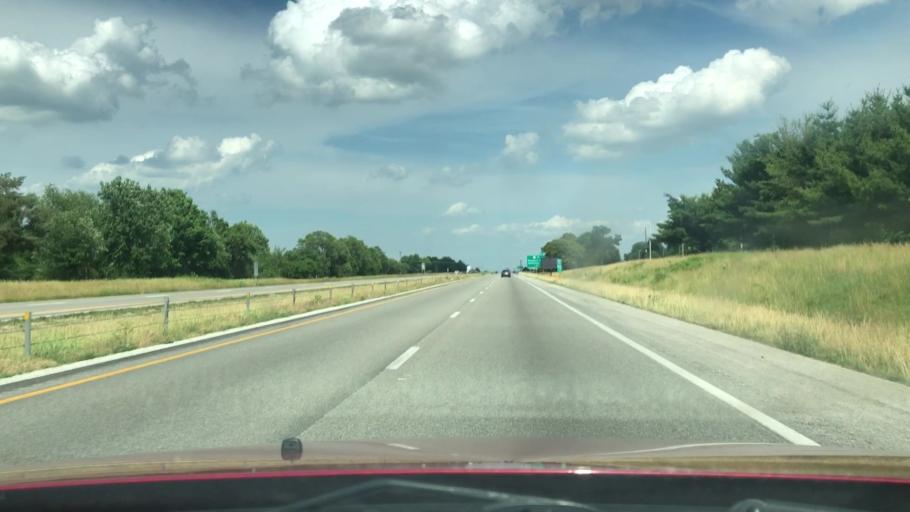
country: US
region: Missouri
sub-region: Greene County
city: Springfield
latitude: 37.2502
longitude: -93.2818
